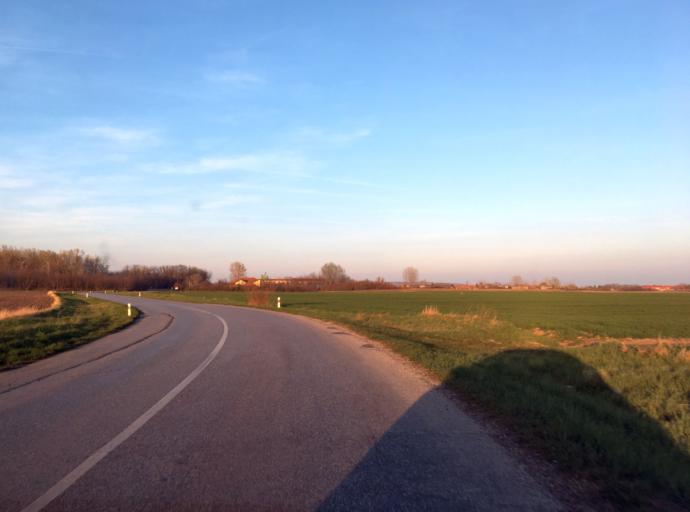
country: SK
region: Nitriansky
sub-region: Okres Komarno
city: Hurbanovo
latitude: 47.8089
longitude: 18.2086
